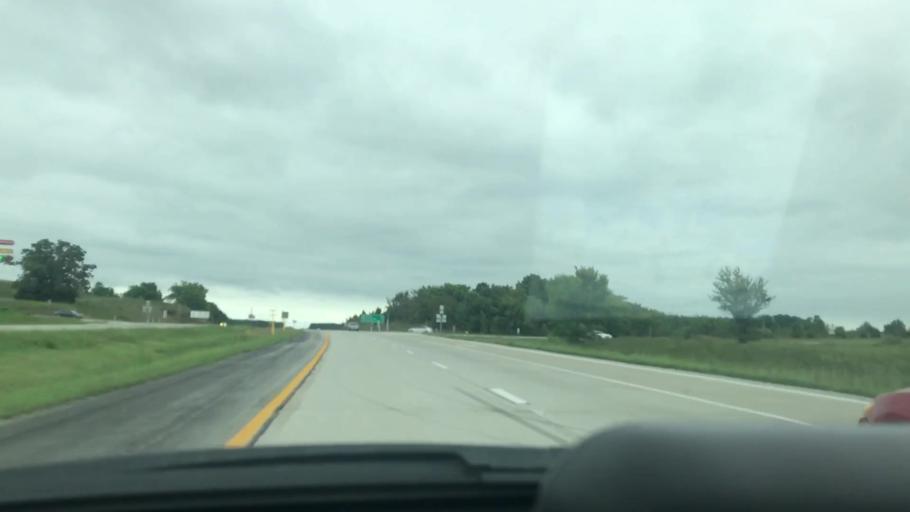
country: US
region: Missouri
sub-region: Greene County
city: Fair Grove
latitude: 37.4582
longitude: -93.1398
